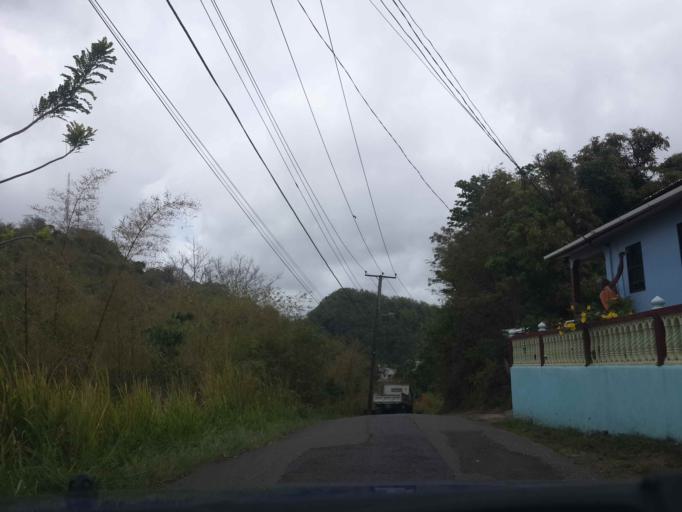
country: LC
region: Castries Quarter
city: Castries
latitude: 13.9945
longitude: -60.9793
